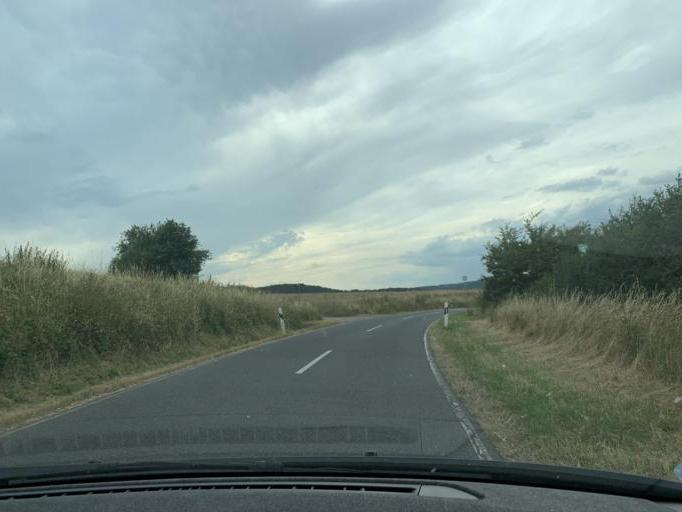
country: DE
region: North Rhine-Westphalia
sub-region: Regierungsbezirk Koln
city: Nideggen
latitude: 50.7172
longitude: 6.4834
